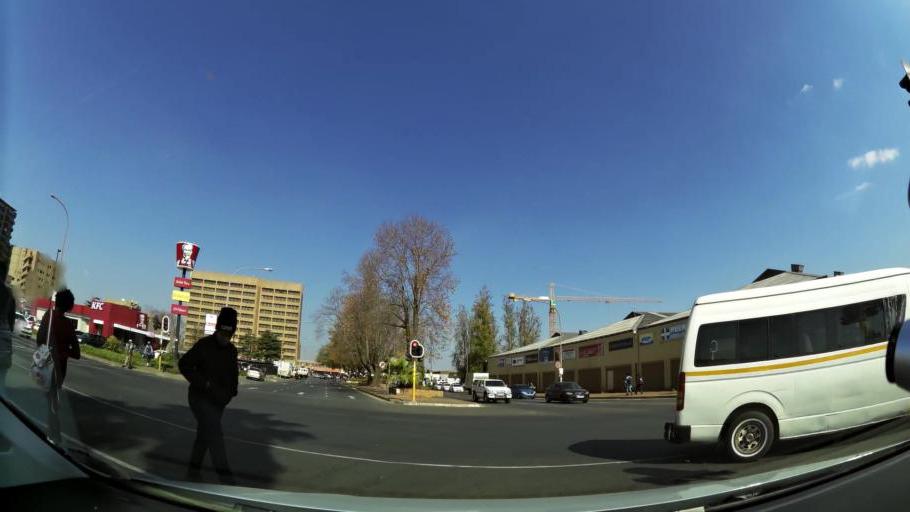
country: ZA
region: Gauteng
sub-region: City of Johannesburg Metropolitan Municipality
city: Modderfontein
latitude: -26.1055
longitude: 28.2317
